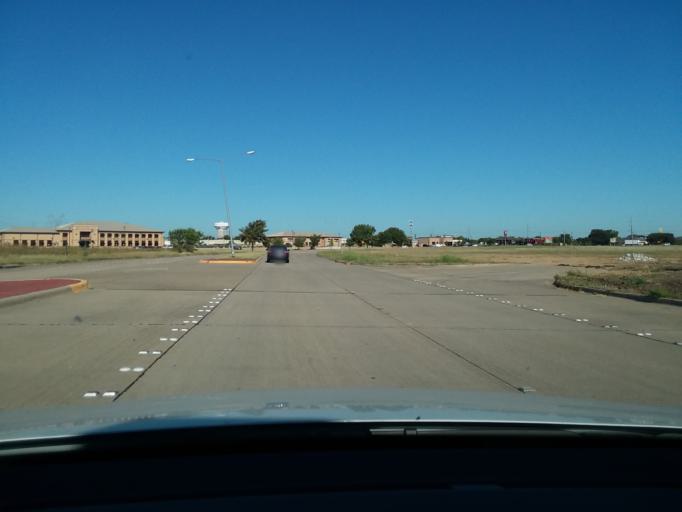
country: US
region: Texas
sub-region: Denton County
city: Lewisville
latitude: 33.0677
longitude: -97.0212
